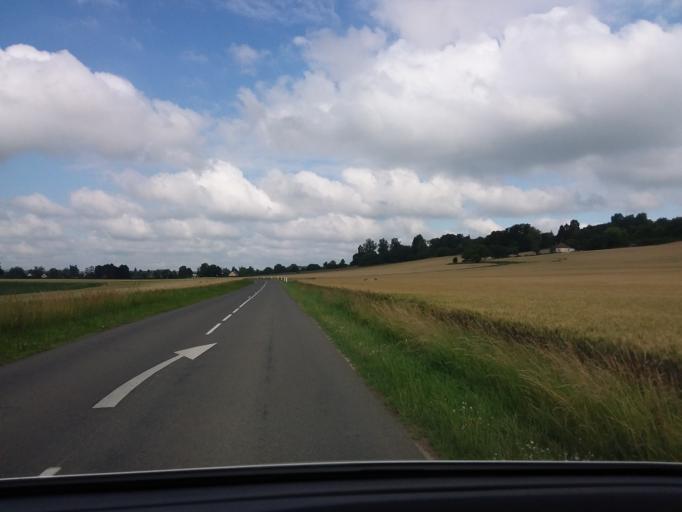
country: FR
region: Champagne-Ardenne
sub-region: Departement de la Marne
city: Fismes
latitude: 49.3884
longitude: 3.7495
